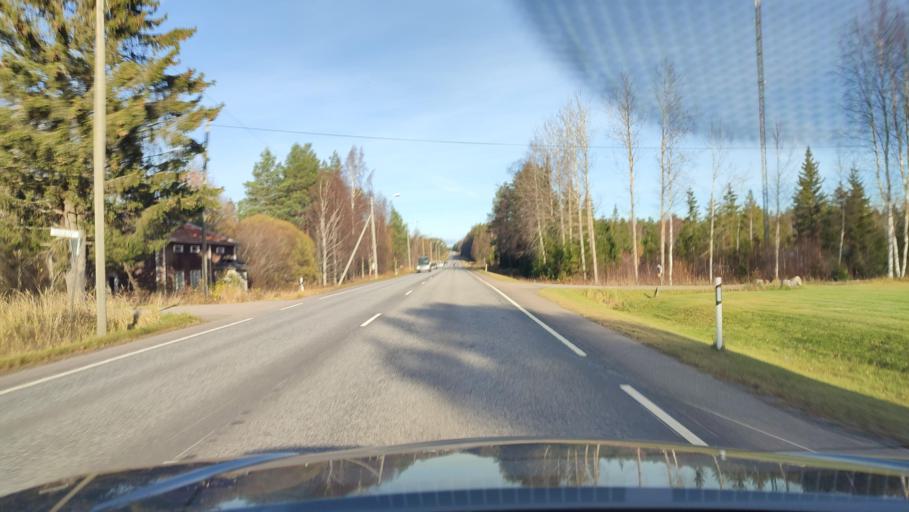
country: FI
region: Ostrobothnia
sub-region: Vaasa
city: Malax
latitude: 62.8060
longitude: 21.6796
